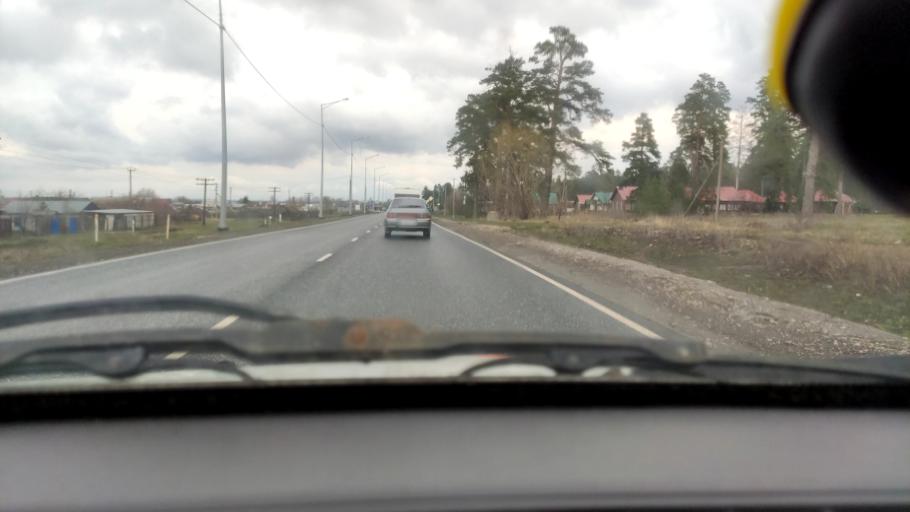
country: RU
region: Samara
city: Zhigulevsk
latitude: 53.5809
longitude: 49.5651
